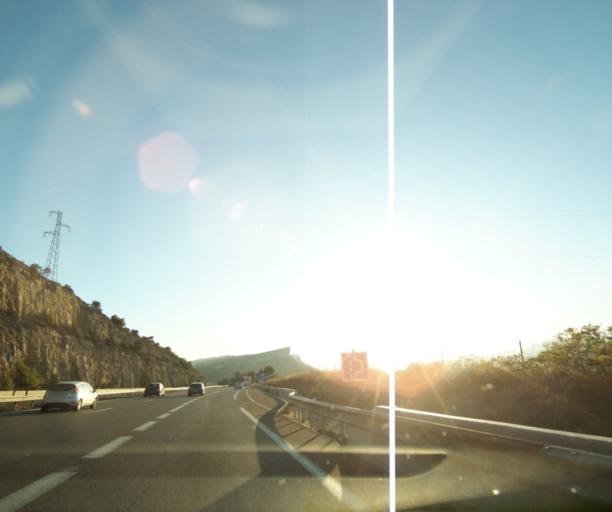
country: FR
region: Provence-Alpes-Cote d'Azur
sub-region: Departement des Bouches-du-Rhone
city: Roquefort-la-Bedoule
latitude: 43.2309
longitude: 5.5860
